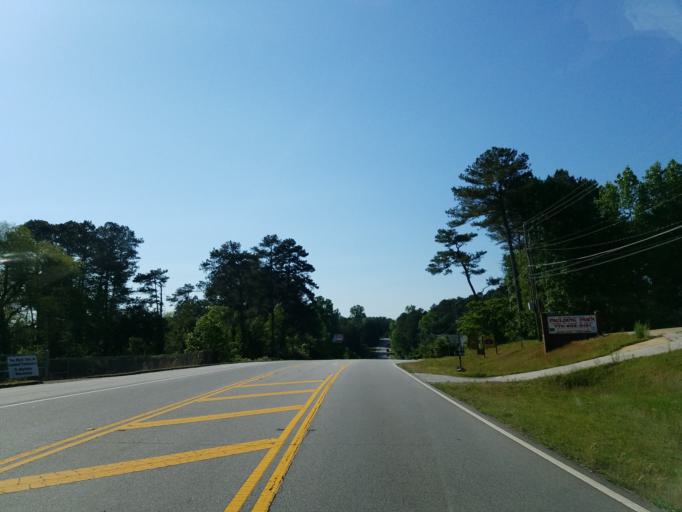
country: US
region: Georgia
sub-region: Paulding County
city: Dallas
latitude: 33.9138
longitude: -84.8242
